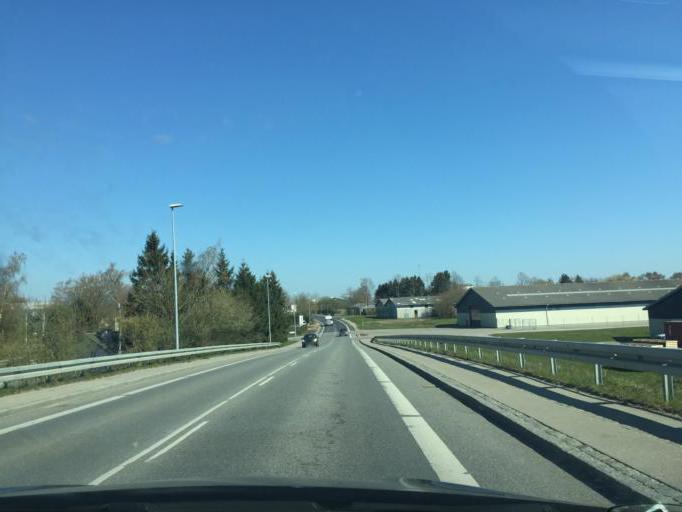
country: DK
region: South Denmark
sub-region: Faaborg-Midtfyn Kommune
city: Ringe
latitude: 55.2450
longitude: 10.4848
